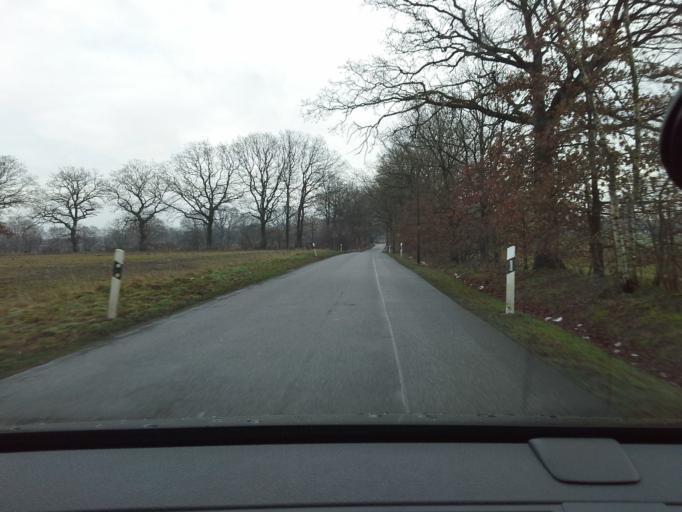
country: DE
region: Schleswig-Holstein
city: Henstedt-Ulzburg
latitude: 53.7457
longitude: 10.0189
